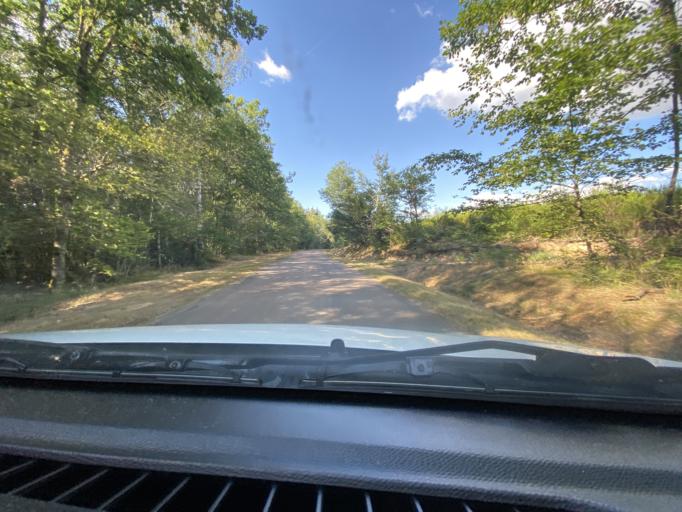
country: FR
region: Bourgogne
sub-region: Departement de la Cote-d'Or
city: Saulieu
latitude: 47.3028
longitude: 4.1783
